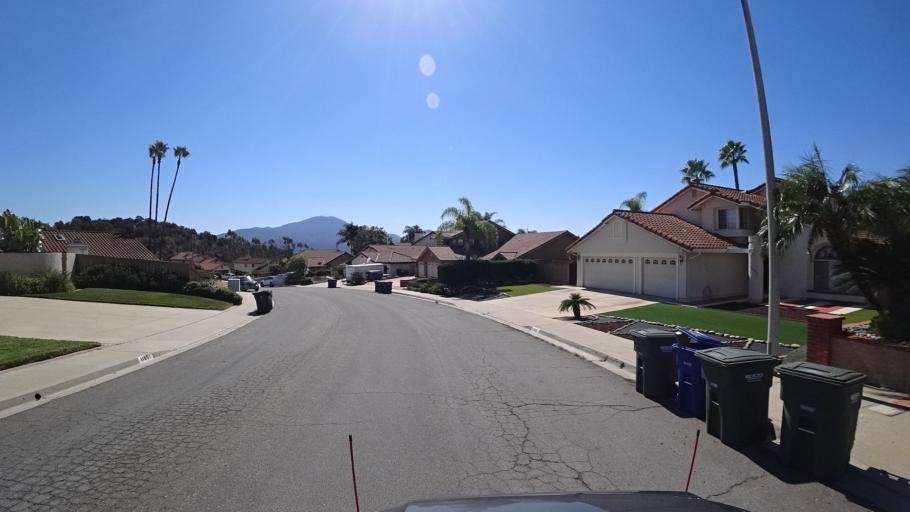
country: US
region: California
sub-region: San Diego County
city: Rancho San Diego
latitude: 32.7552
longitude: -116.9396
